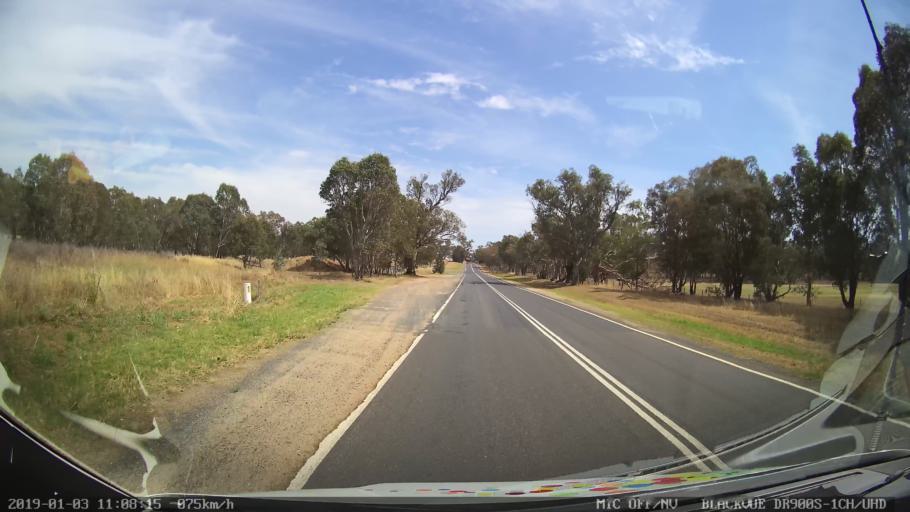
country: AU
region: New South Wales
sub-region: Young
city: Young
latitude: -34.2514
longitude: 148.2579
